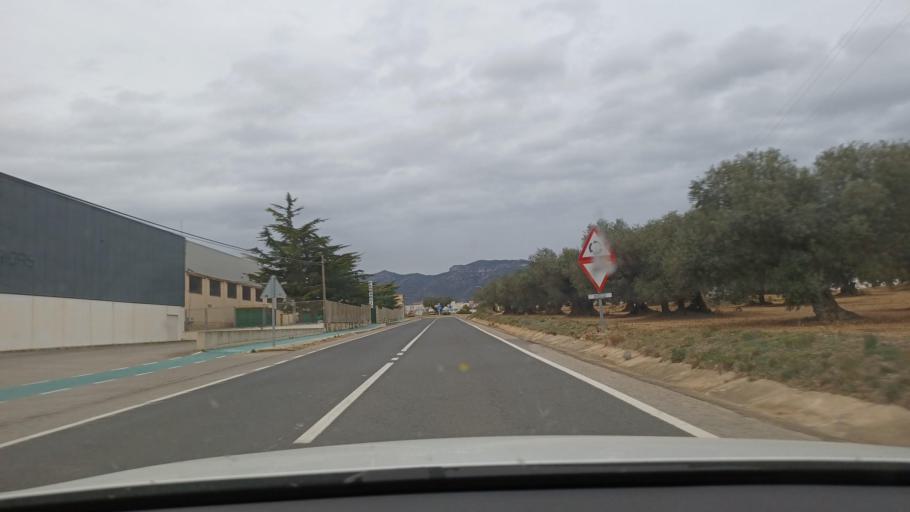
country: ES
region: Valencia
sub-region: Provincia de Castello
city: Rosell
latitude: 40.6309
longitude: 0.2947
